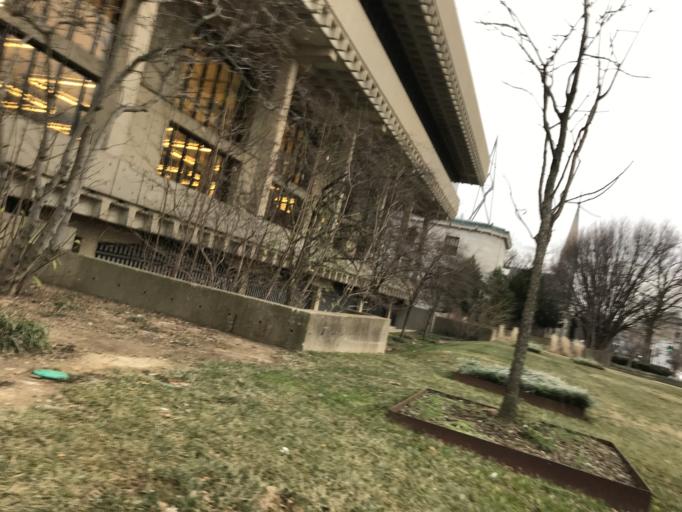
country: US
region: Kentucky
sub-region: Jefferson County
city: Louisville
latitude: 38.2452
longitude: -85.7583
